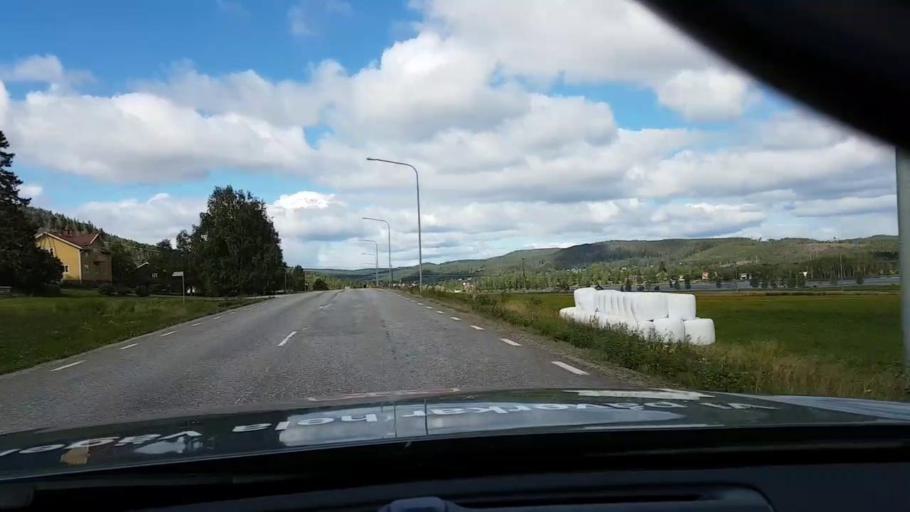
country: SE
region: Vaesternorrland
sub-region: OErnskoeldsviks Kommun
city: Bredbyn
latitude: 63.5000
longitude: 18.0799
